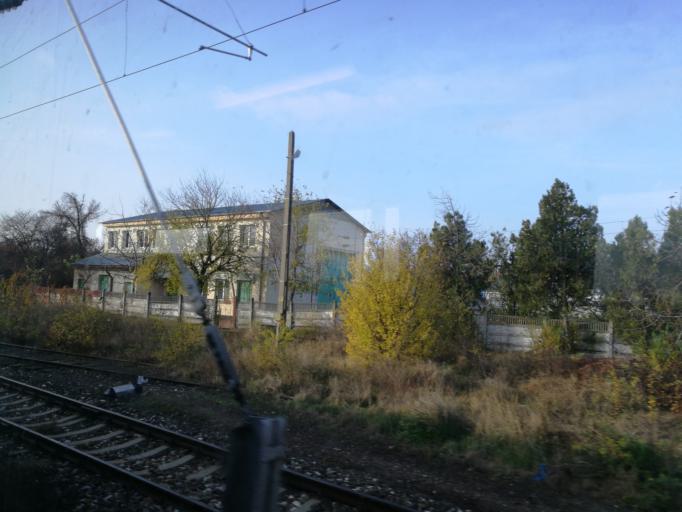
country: RO
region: Buzau
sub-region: Municipiul Ramnicu Sarat
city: Ramnicu Sarat
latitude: 45.3817
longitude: 27.0576
